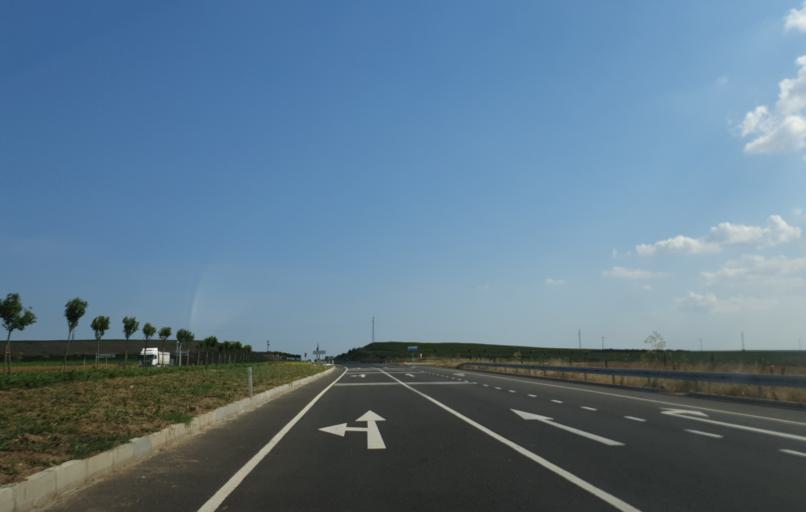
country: TR
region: Tekirdag
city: Muratli
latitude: 41.2121
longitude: 27.5340
